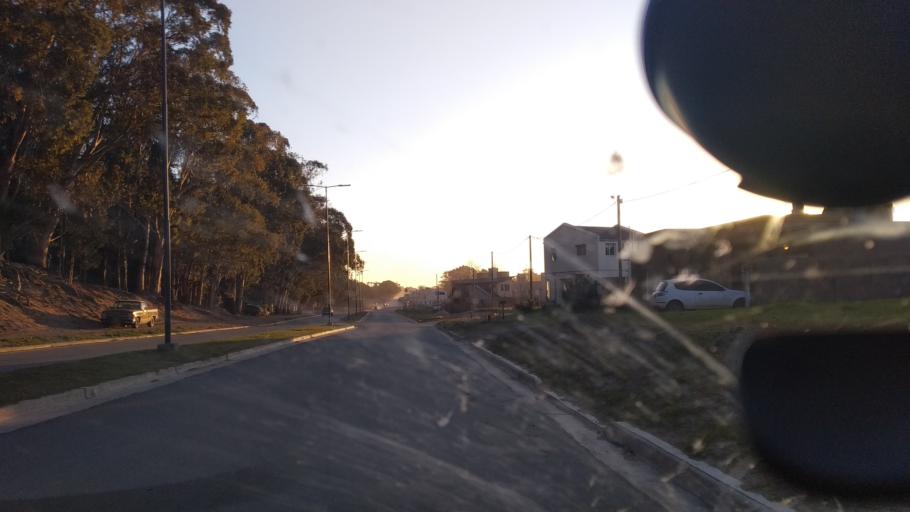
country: AR
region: Buenos Aires
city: Necochea
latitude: -38.5859
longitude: -58.7518
